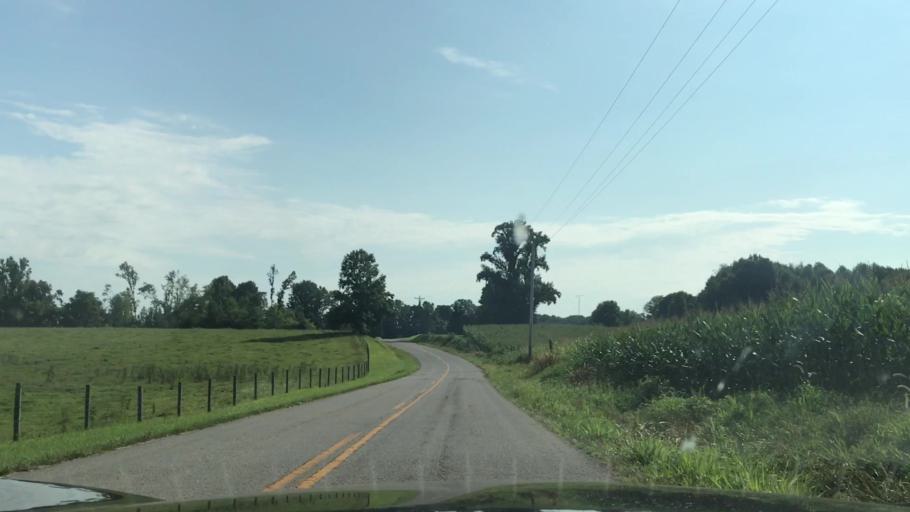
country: US
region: Kentucky
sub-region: Hart County
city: Horse Cave
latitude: 37.1890
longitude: -85.7630
